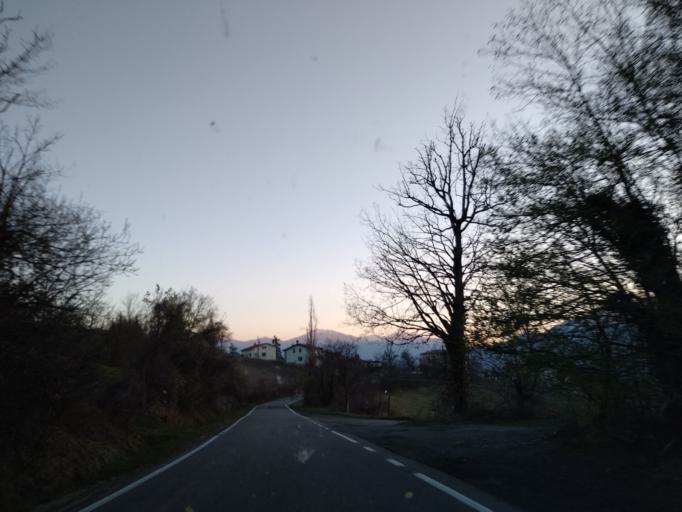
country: IT
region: Emilia-Romagna
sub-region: Provincia di Reggio Emilia
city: Castelnovo ne'Monti
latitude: 44.4173
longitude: 10.4031
